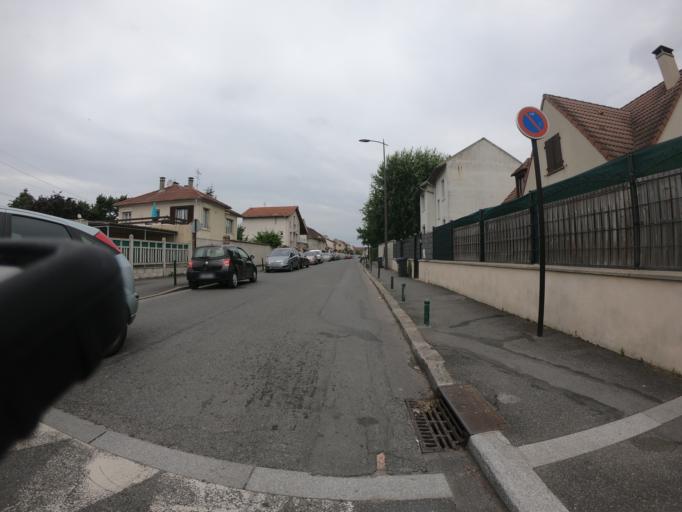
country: FR
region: Ile-de-France
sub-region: Departement du Val-de-Marne
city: Thiais
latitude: 48.7605
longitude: 2.3868
